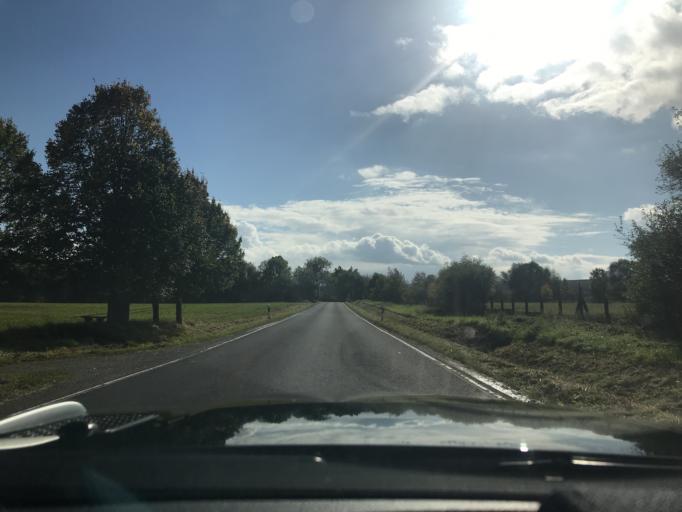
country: DE
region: Thuringia
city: Oberdorla
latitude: 51.1723
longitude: 10.3970
